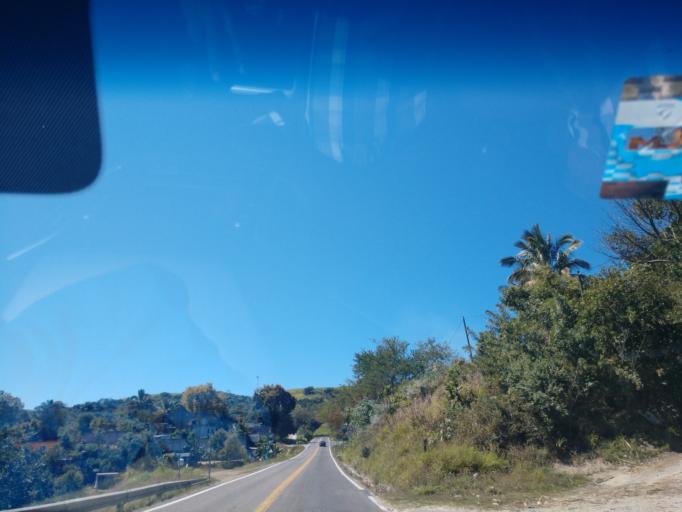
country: MX
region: Nayarit
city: Xalisco
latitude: 21.3660
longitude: -104.9161
